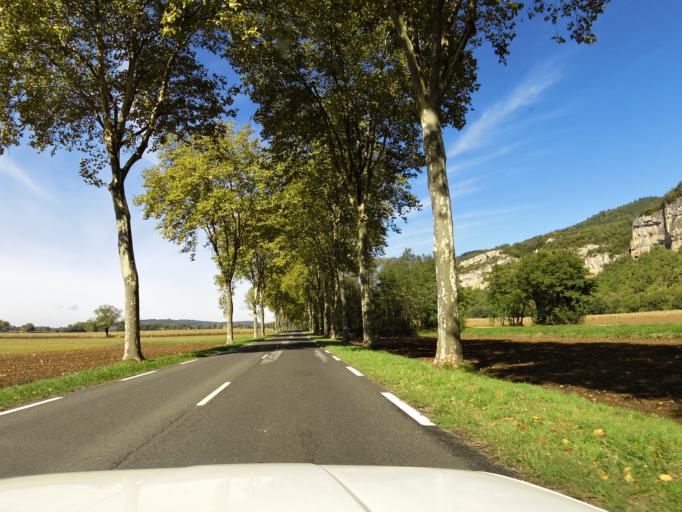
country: FR
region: Rhone-Alpes
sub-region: Departement de l'Ain
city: Saint-Sorlin-en-Bugey
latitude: 45.8696
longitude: 5.3891
